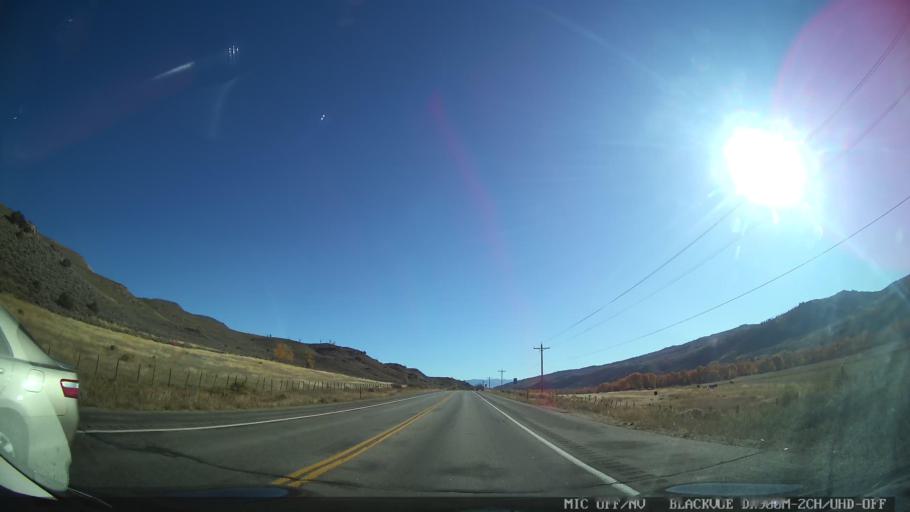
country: US
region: Colorado
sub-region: Grand County
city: Hot Sulphur Springs
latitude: 40.0956
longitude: -106.0571
